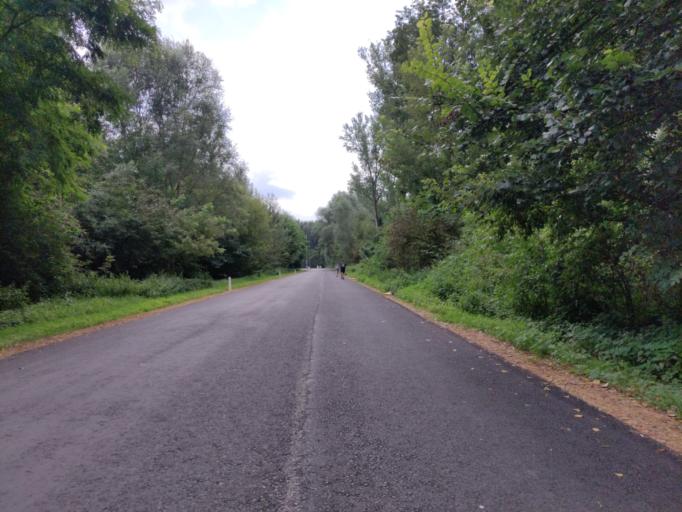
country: AT
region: Lower Austria
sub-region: Politischer Bezirk Melk
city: Melk
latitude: 48.2310
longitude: 15.3276
